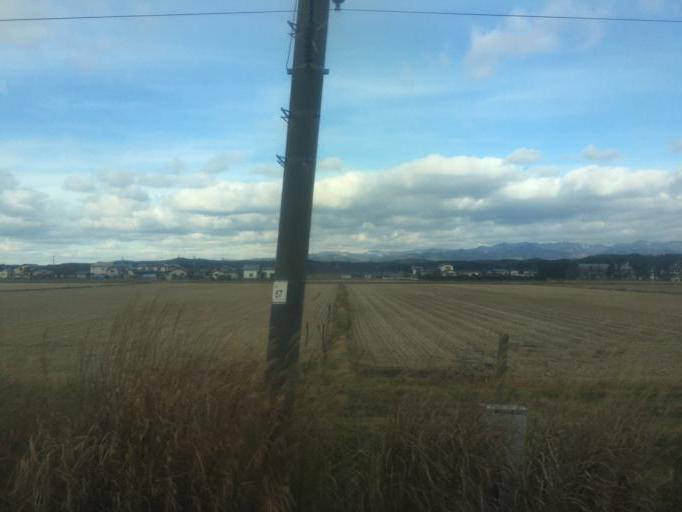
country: JP
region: Akita
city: Noshiromachi
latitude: 40.2156
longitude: 140.1642
